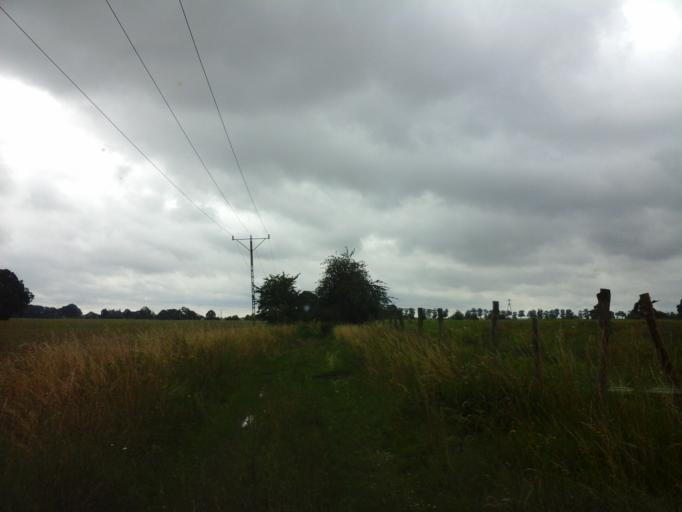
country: PL
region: West Pomeranian Voivodeship
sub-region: Powiat choszczenski
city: Krzecin
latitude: 52.9848
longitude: 15.4841
